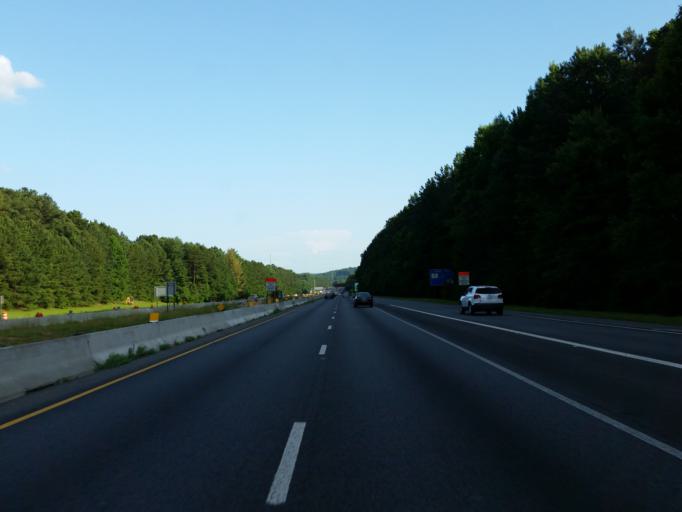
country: US
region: Georgia
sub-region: Cobb County
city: Kennesaw
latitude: 34.0337
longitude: -84.5619
